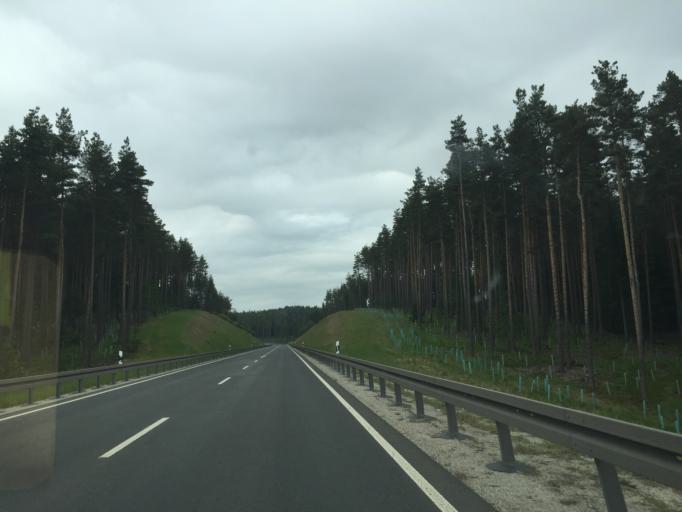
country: DE
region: Thuringia
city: Langewiesen
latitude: 50.6925
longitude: 10.9706
